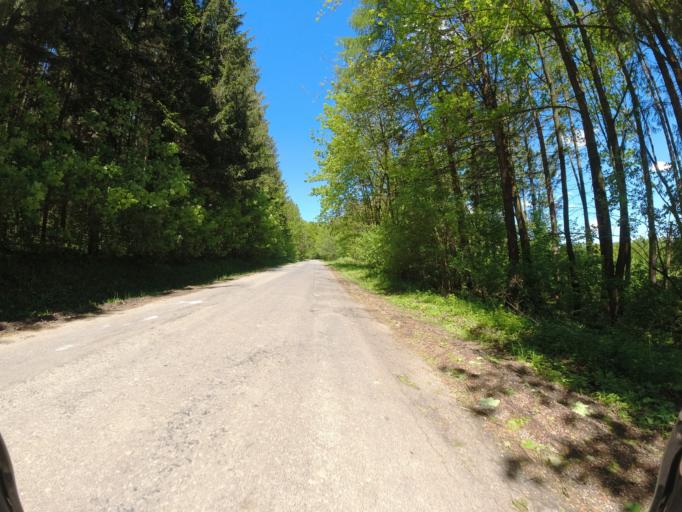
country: CZ
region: Zlin
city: Strani
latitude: 48.9192
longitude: 17.7056
